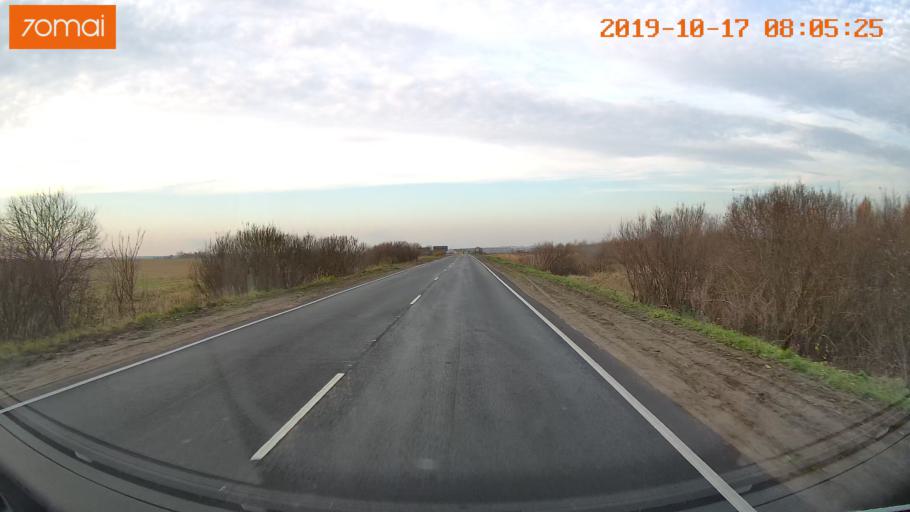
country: RU
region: Vladimir
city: Kol'chugino
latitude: 56.3348
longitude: 39.4159
